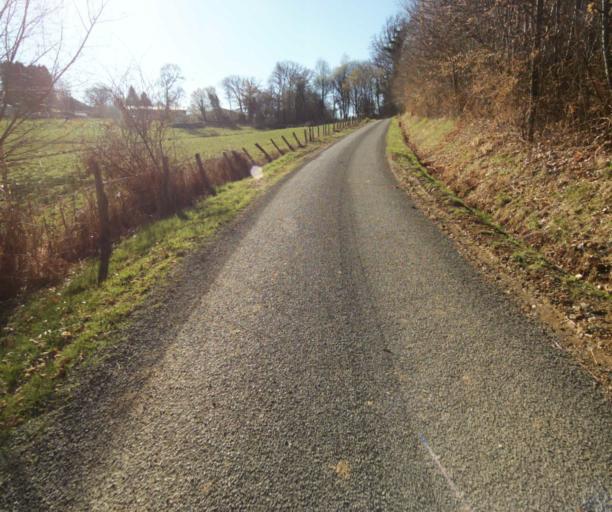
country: FR
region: Limousin
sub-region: Departement de la Correze
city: Seilhac
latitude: 45.4007
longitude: 1.7222
